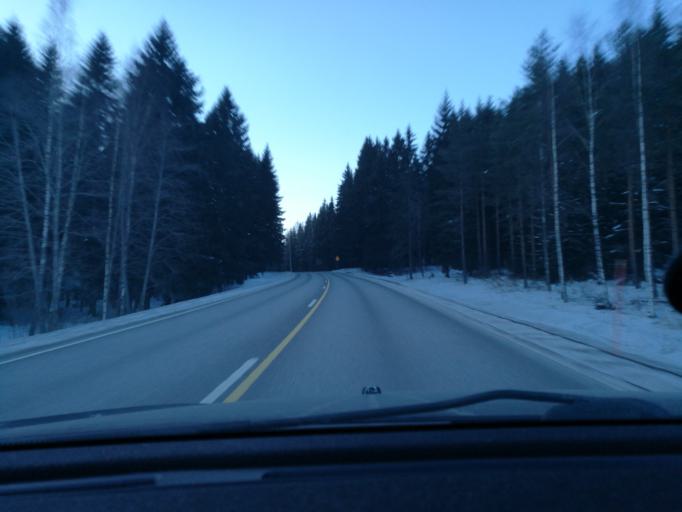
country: FI
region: Uusimaa
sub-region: Helsinki
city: Vihti
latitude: 60.3862
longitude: 24.5117
